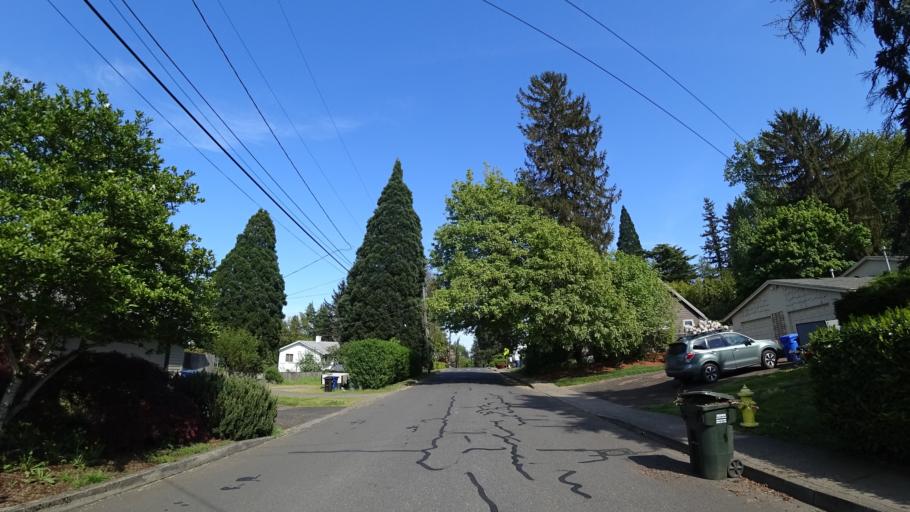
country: US
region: Oregon
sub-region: Clackamas County
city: Milwaukie
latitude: 45.4549
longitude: -122.6266
